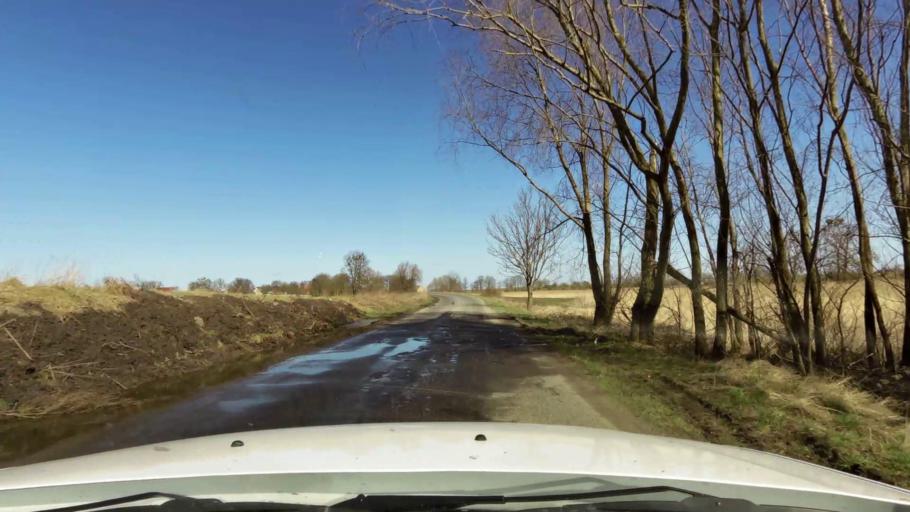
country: PL
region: West Pomeranian Voivodeship
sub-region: Powiat gryfinski
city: Cedynia
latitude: 52.8790
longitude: 14.2862
